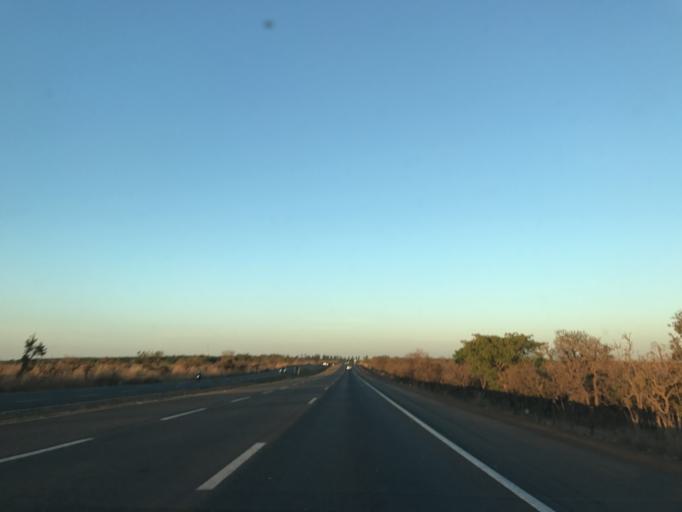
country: BR
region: Goias
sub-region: Abadiania
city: Abadiania
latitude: -16.1956
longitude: -48.7307
